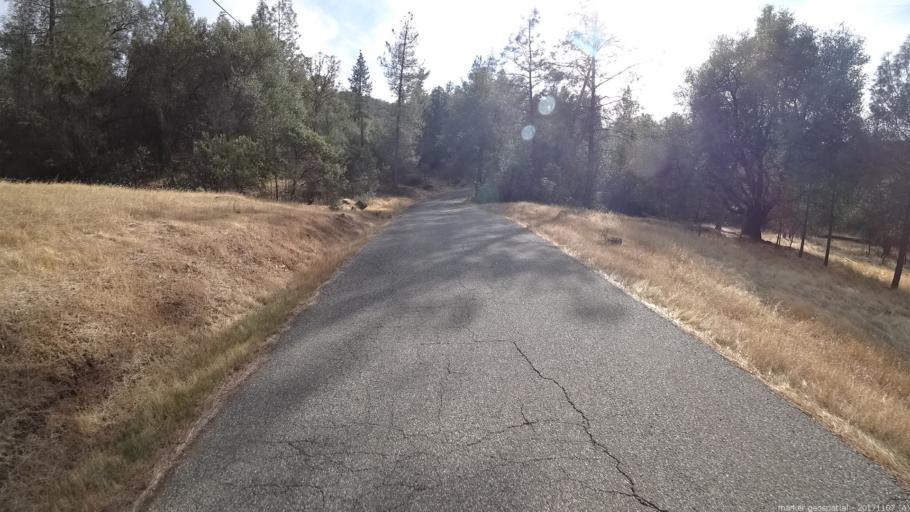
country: US
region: California
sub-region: Shasta County
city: Shasta
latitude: 40.5348
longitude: -122.5261
